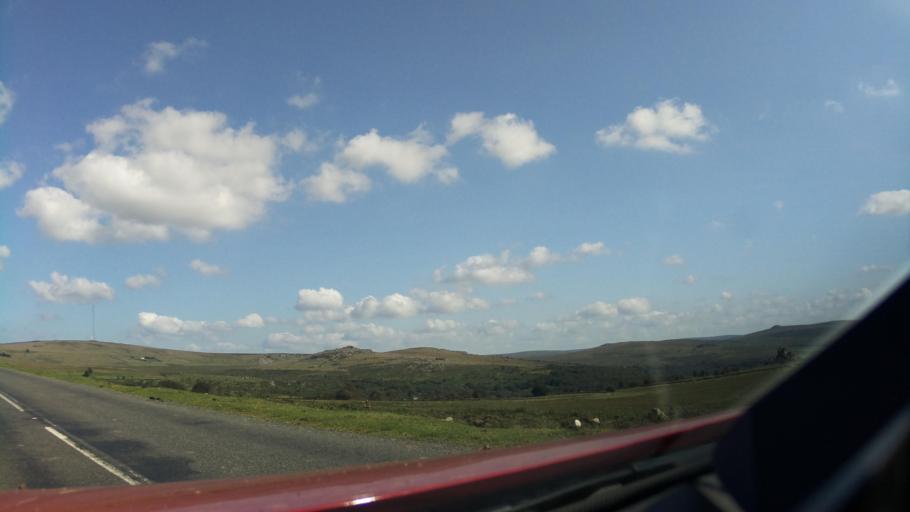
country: GB
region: England
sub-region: Devon
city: Horrabridge
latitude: 50.5563
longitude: -4.0641
